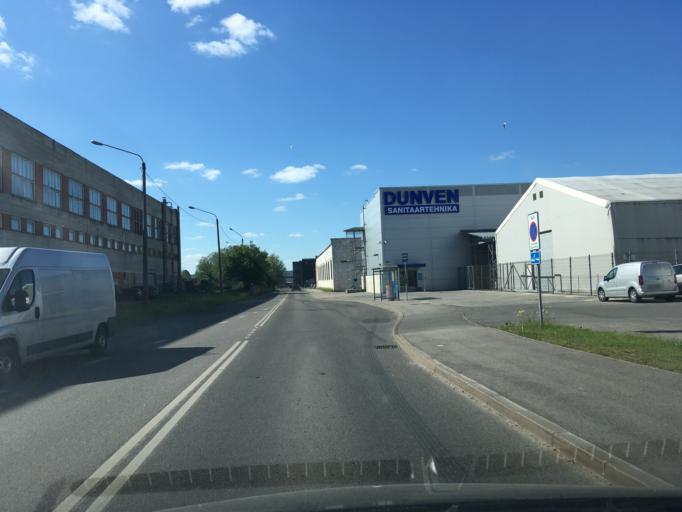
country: EE
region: Harju
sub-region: Tallinna linn
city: Tallinn
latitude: 59.4225
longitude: 24.8110
